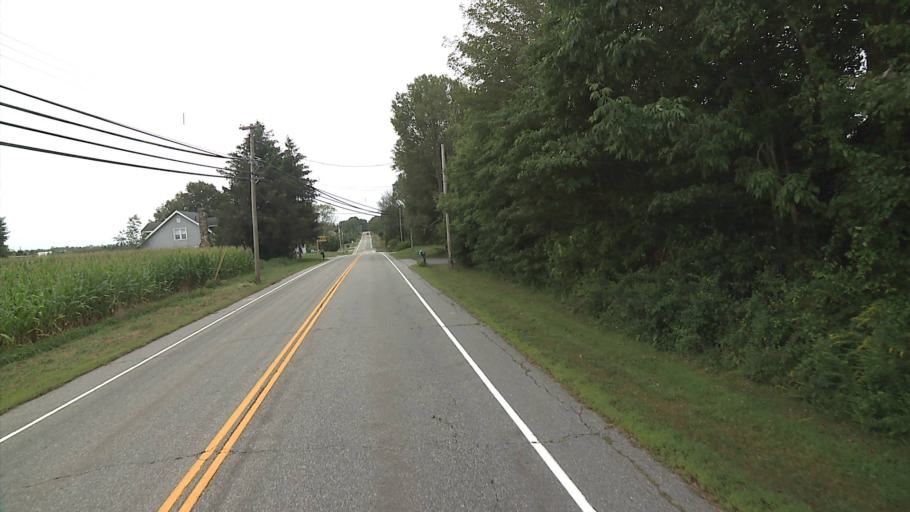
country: US
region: Connecticut
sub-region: Hartford County
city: Manchester
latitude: 41.7428
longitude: -72.4370
